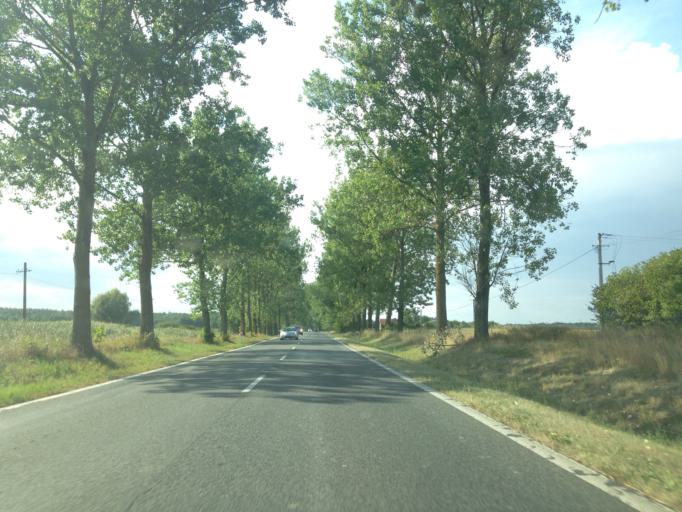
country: PL
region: Kujawsko-Pomorskie
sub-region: Powiat swiecki
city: Bukowiec
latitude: 53.4617
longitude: 18.1850
